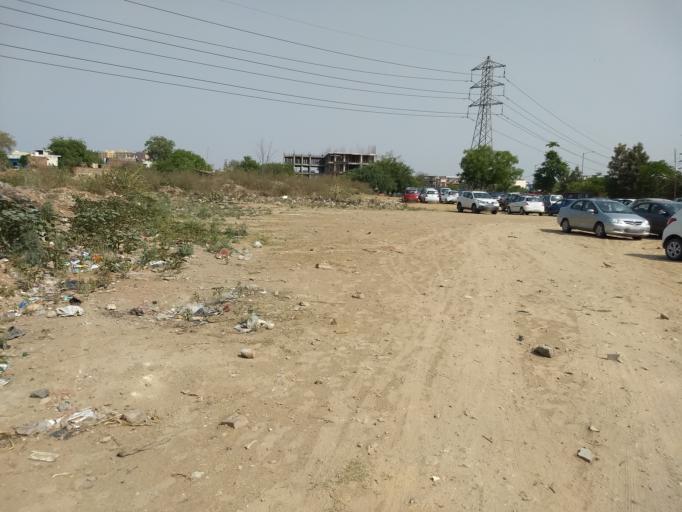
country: IN
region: Haryana
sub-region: Gurgaon
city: Gurgaon
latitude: 28.4481
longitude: 77.0440
